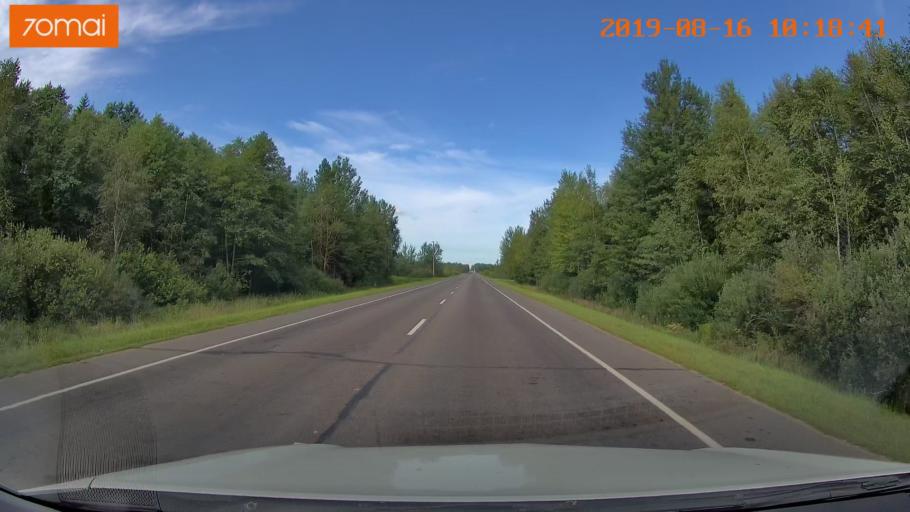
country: BY
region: Mogilev
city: Asipovichy
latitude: 53.3060
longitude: 28.6842
